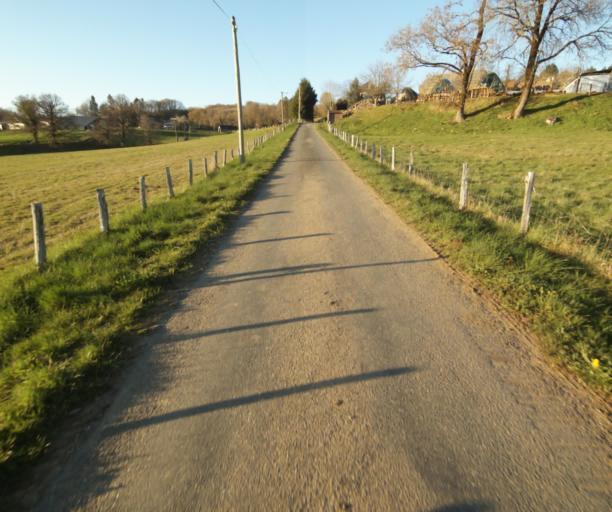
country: FR
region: Limousin
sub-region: Departement de la Correze
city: Saint-Clement
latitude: 45.3311
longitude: 1.7162
